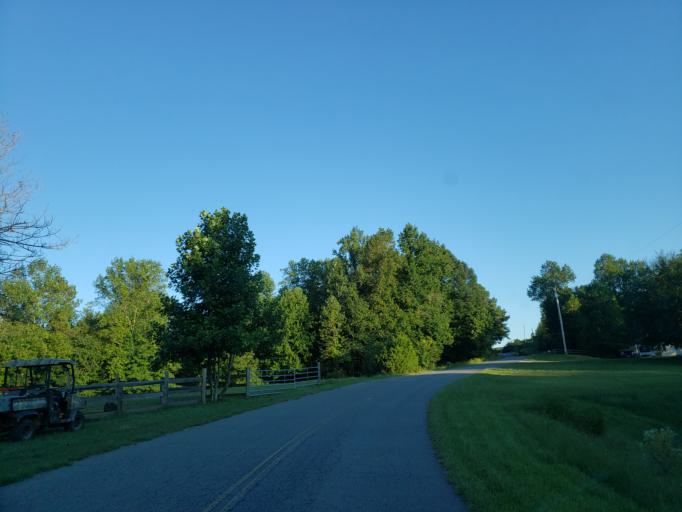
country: US
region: Georgia
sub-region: Bartow County
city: Rydal
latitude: 34.3960
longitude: -84.6701
